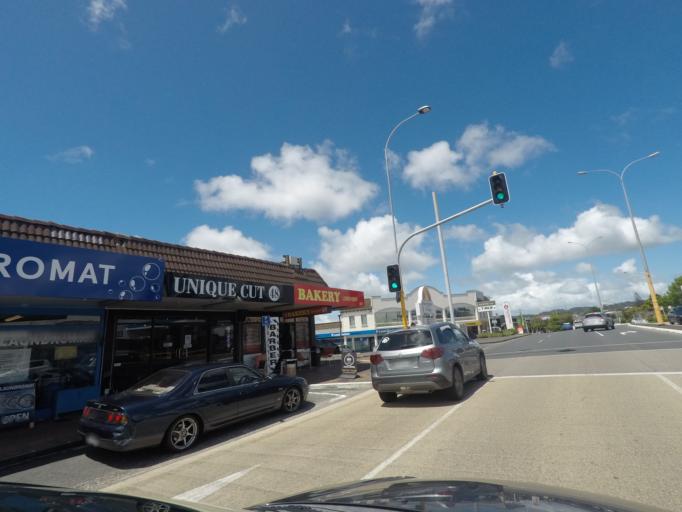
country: NZ
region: Auckland
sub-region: Auckland
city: Rosebank
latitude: -36.8865
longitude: 174.6444
